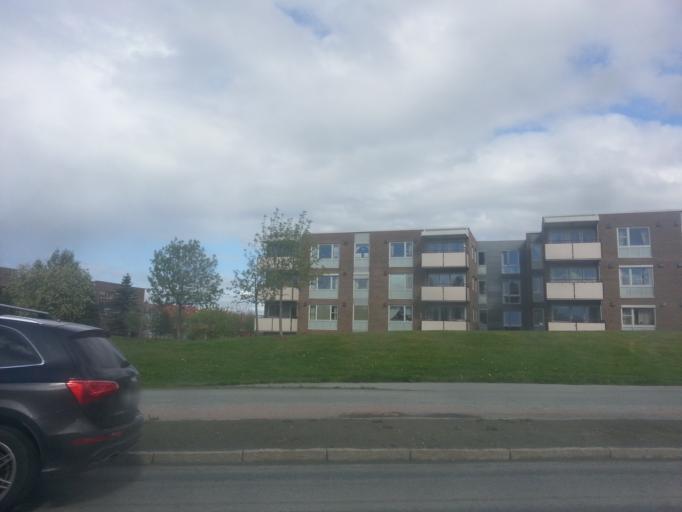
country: NO
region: Sor-Trondelag
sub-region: Trondheim
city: Trondheim
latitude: 63.4129
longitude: 10.4327
